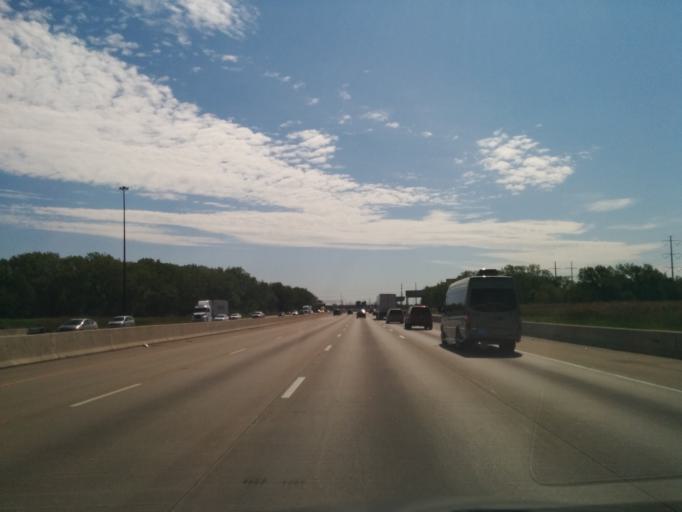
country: US
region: Indiana
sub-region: Lake County
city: Gary
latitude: 41.5673
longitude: -87.3363
